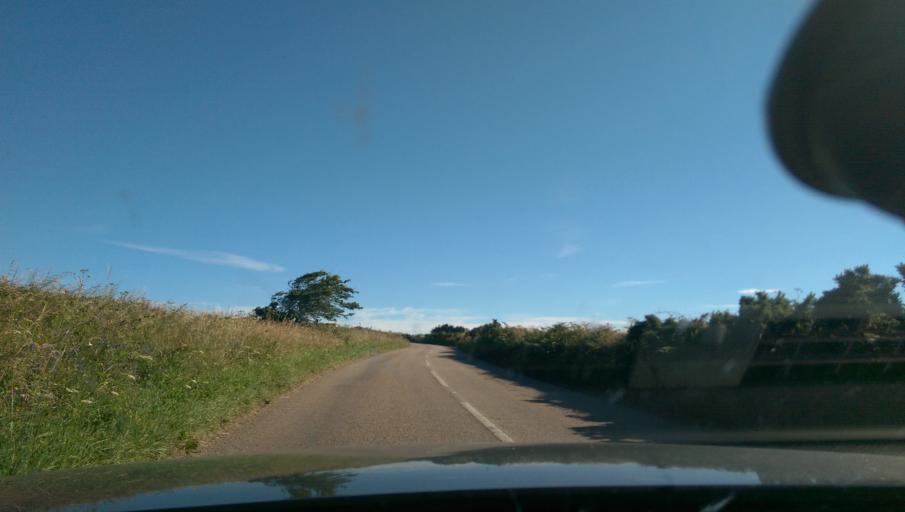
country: GB
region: England
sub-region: Cornwall
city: Penzance
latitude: 50.1495
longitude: -5.5188
